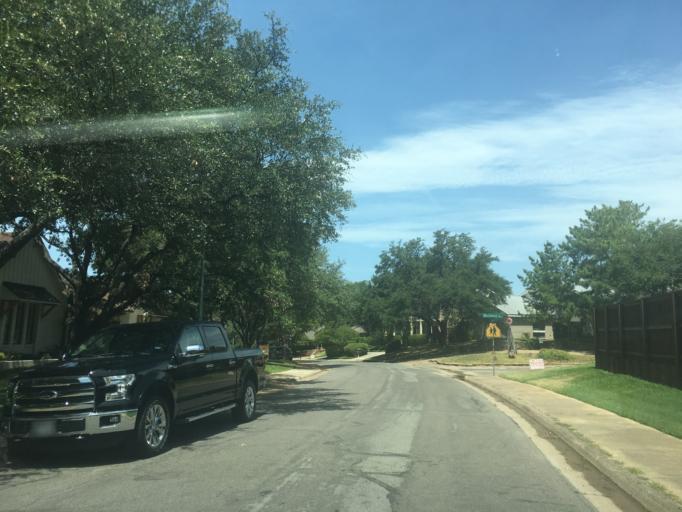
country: US
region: Texas
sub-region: Dallas County
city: Richardson
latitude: 32.8840
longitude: -96.7398
